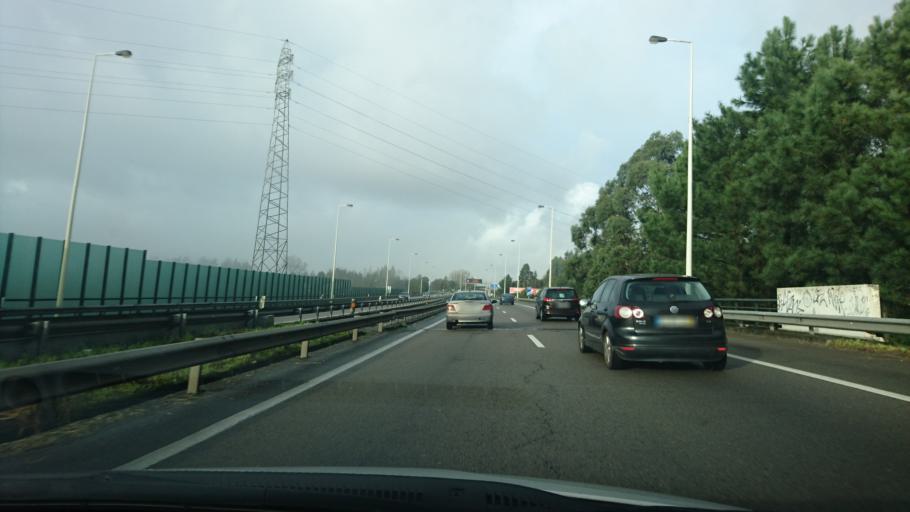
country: PT
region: Porto
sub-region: Gondomar
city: Gondomar
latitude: 41.1549
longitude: -8.5532
